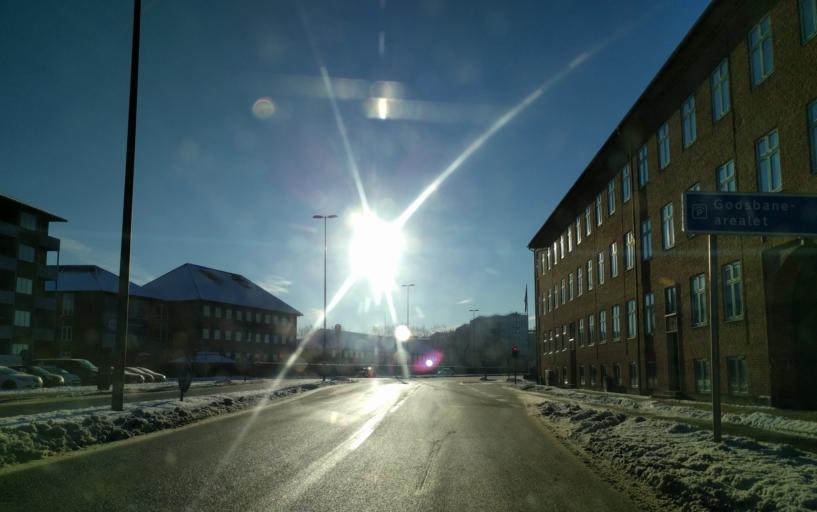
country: DK
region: North Denmark
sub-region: Alborg Kommune
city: Aalborg
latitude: 57.0403
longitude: 9.9314
